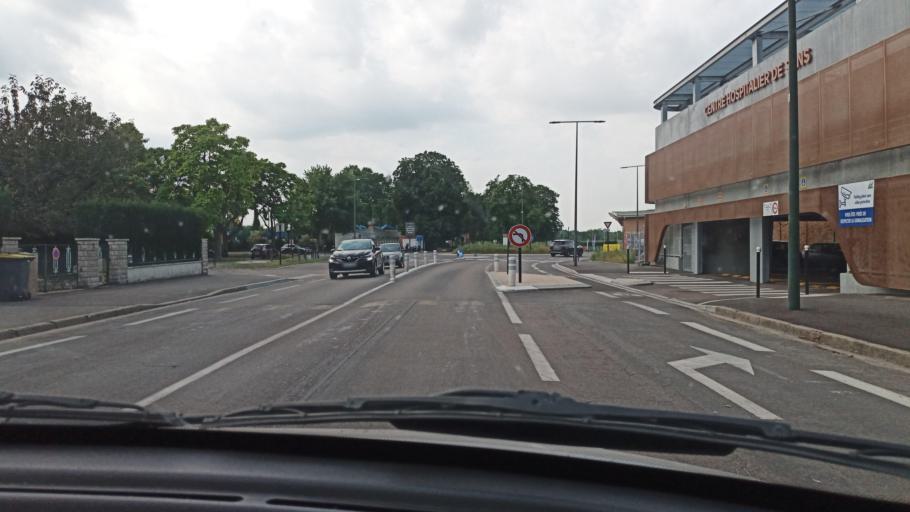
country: FR
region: Bourgogne
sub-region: Departement de l'Yonne
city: Sens
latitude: 48.1918
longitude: 3.2992
